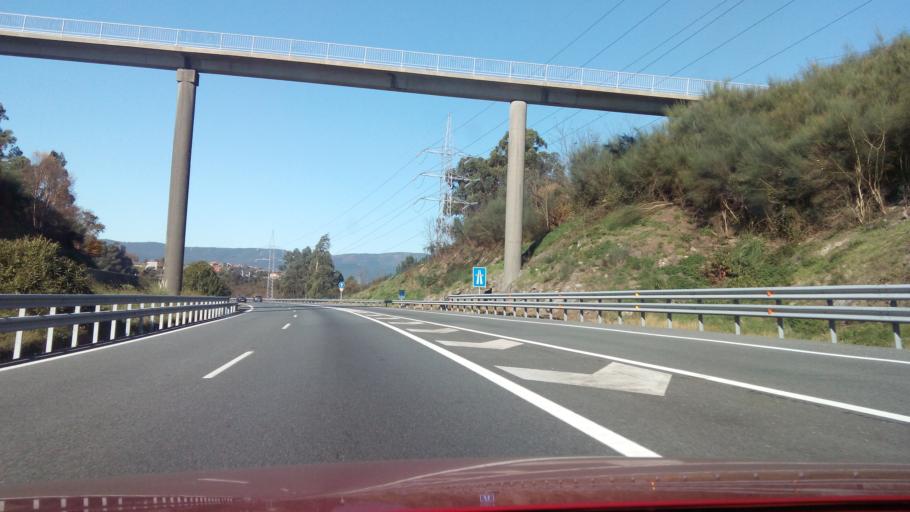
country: ES
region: Galicia
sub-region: Provincia de Pontevedra
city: Pontevedra
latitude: 42.3926
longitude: -8.6418
